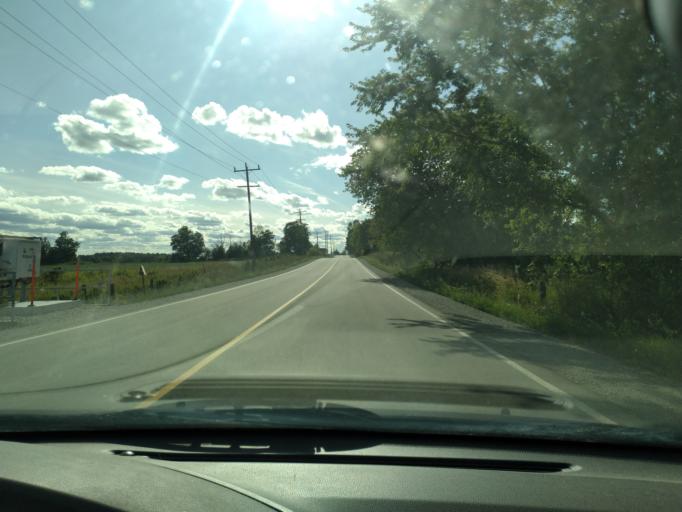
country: CA
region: Ontario
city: Bradford West Gwillimbury
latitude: 44.0791
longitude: -79.6648
